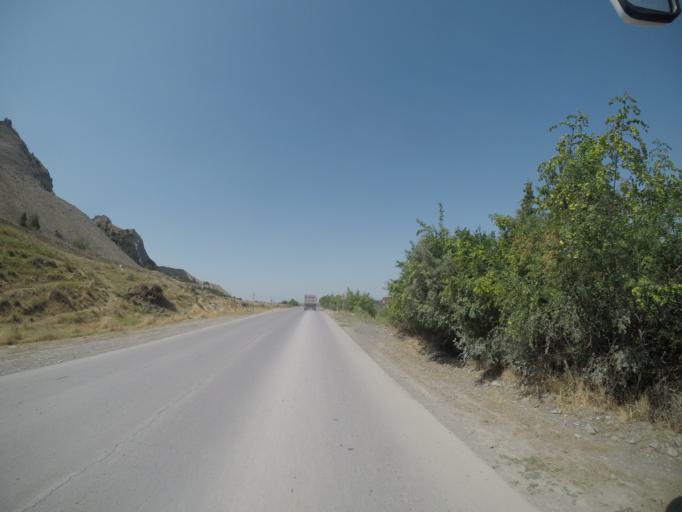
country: AZ
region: Agdas
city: Agdas
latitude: 40.7171
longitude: 47.5581
